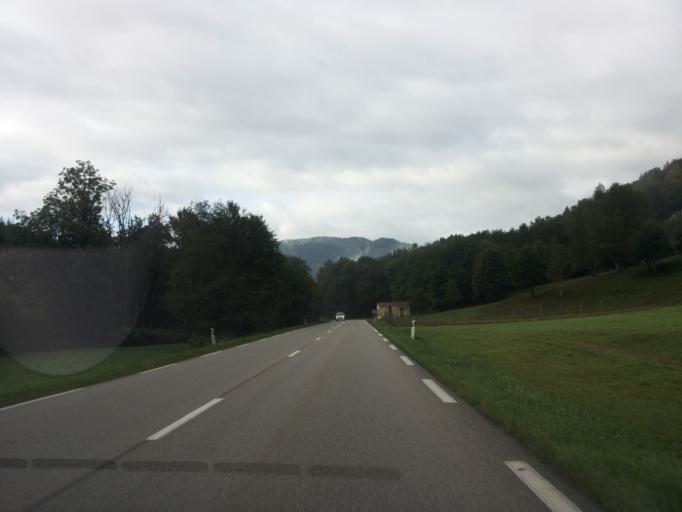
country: FR
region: Lorraine
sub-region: Departement des Vosges
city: Saint-Maurice-sur-Moselle
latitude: 47.8714
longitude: 6.8338
